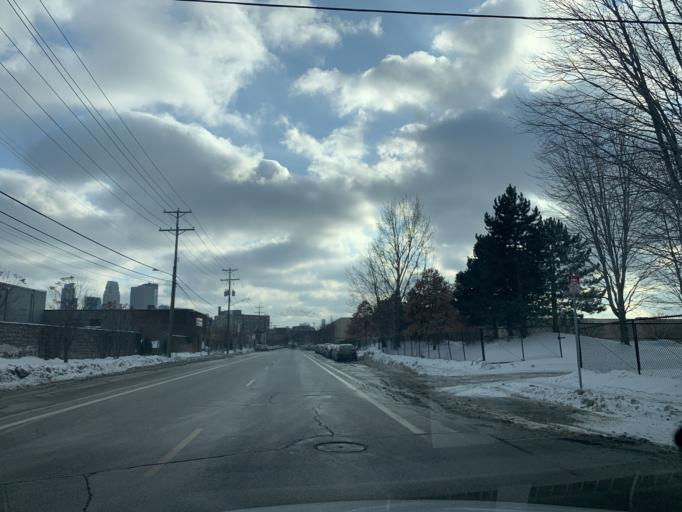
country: US
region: Minnesota
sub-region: Hennepin County
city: Minneapolis
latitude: 44.9954
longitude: -93.2801
